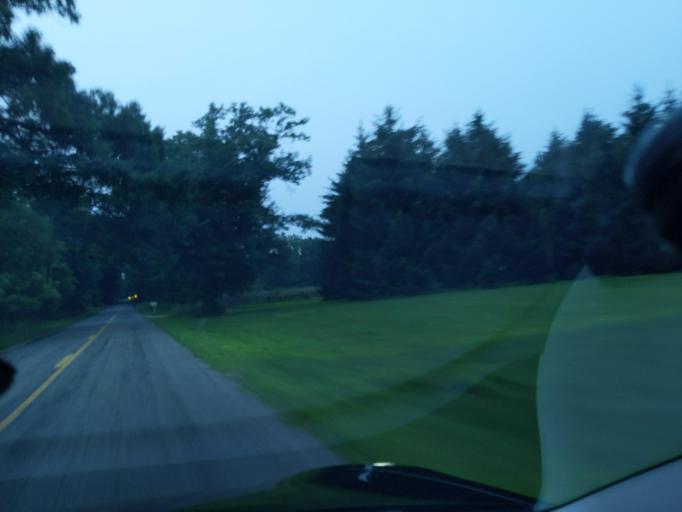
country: US
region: Michigan
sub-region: Eaton County
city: Eaton Rapids
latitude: 42.4611
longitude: -84.5509
